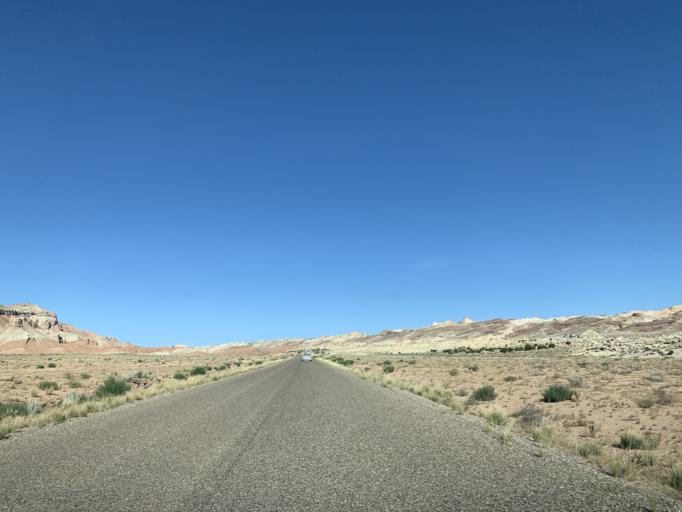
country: US
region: Utah
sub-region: Emery County
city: Ferron
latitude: 38.5781
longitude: -110.7631
